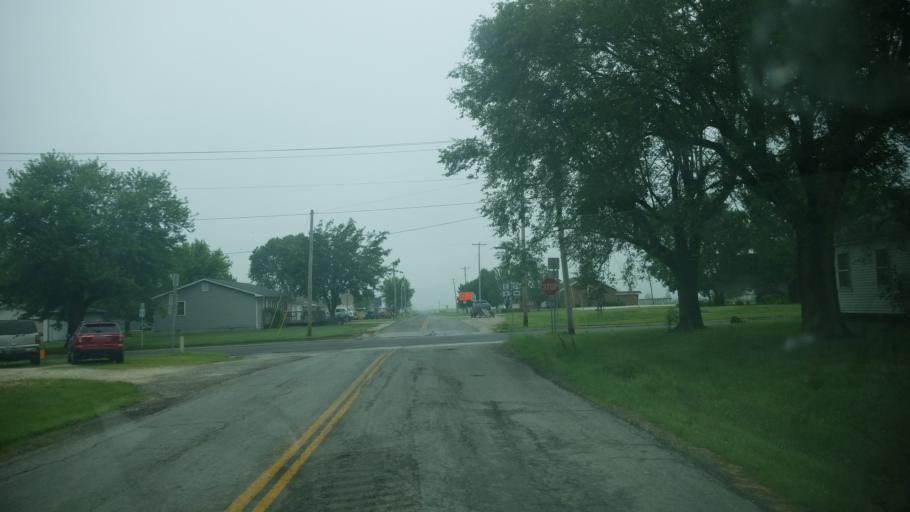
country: US
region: Missouri
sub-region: Audrain County
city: Vandalia
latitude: 39.3451
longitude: -91.3449
